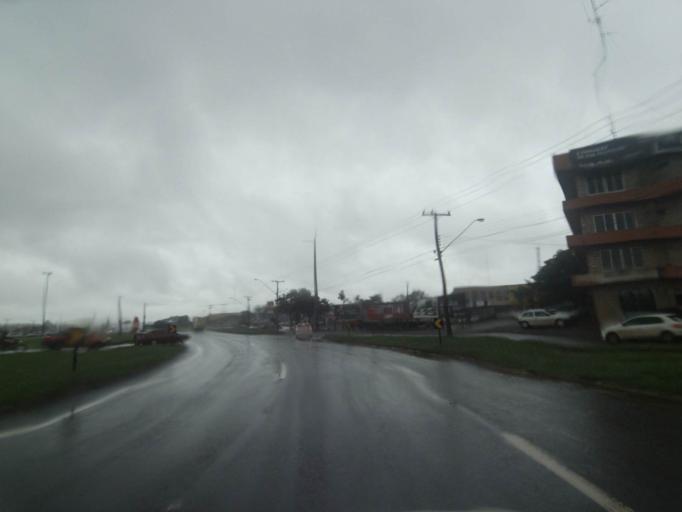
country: BR
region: Parana
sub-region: Foz Do Iguacu
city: Foz do Iguacu
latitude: -25.5107
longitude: -54.5598
